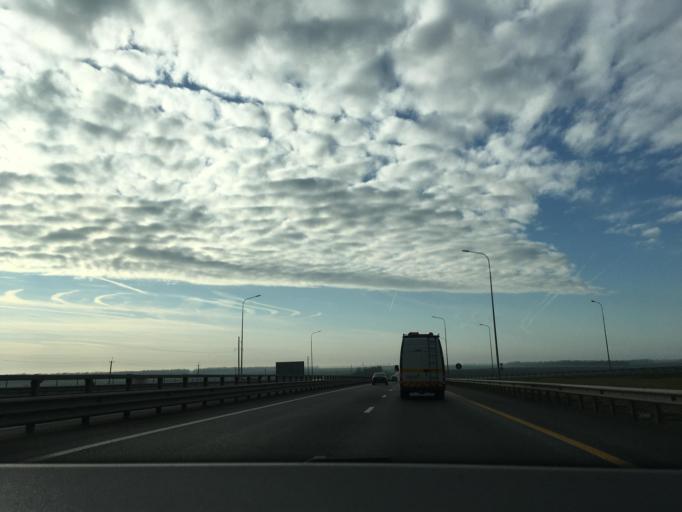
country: RU
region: Krasnodarskiy
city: Irkliyevskaya
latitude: 45.8362
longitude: 39.6767
